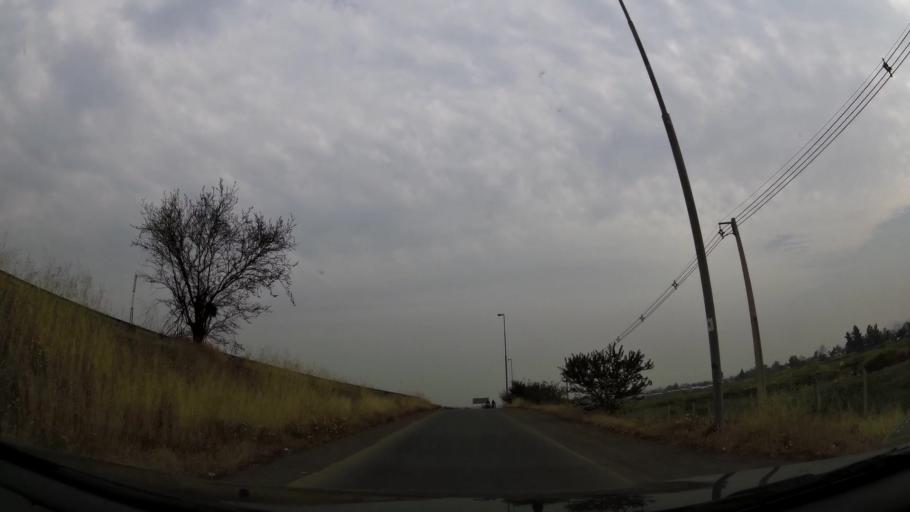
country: CL
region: Santiago Metropolitan
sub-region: Provincia de Chacabuco
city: Chicureo Abajo
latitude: -33.2081
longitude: -70.6683
